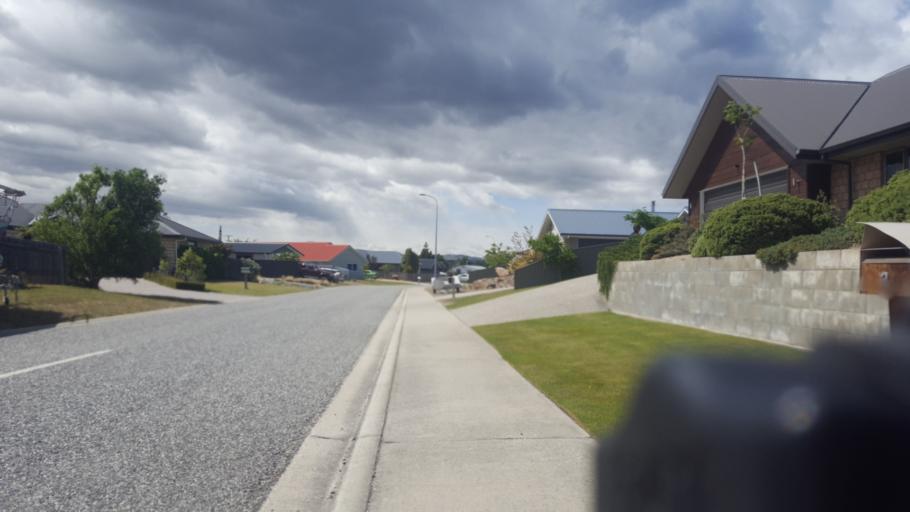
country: NZ
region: Otago
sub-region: Queenstown-Lakes District
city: Wanaka
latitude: -45.1952
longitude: 169.3333
